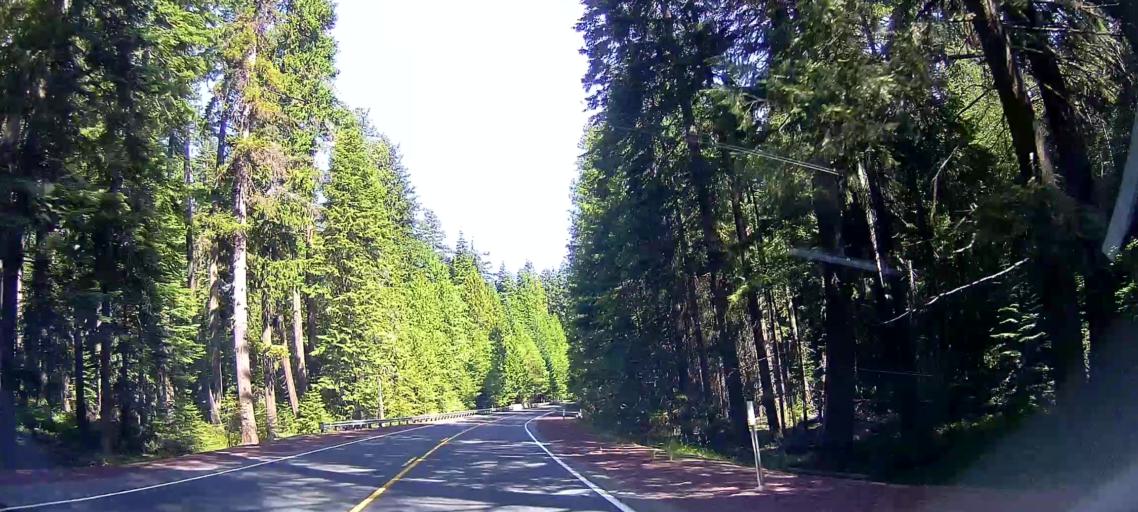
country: US
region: Oregon
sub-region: Jefferson County
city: Warm Springs
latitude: 45.0937
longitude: -121.5517
